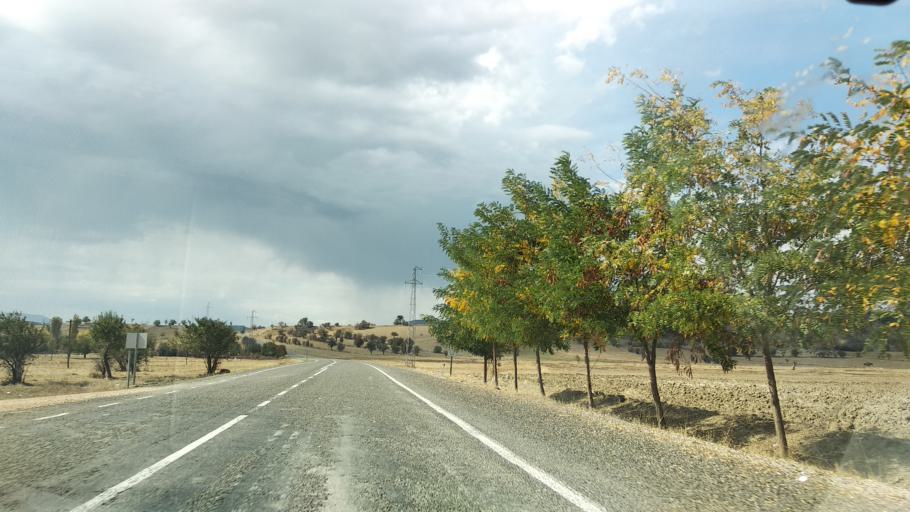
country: TR
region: Bolu
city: Seben
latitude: 40.3767
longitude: 31.5182
